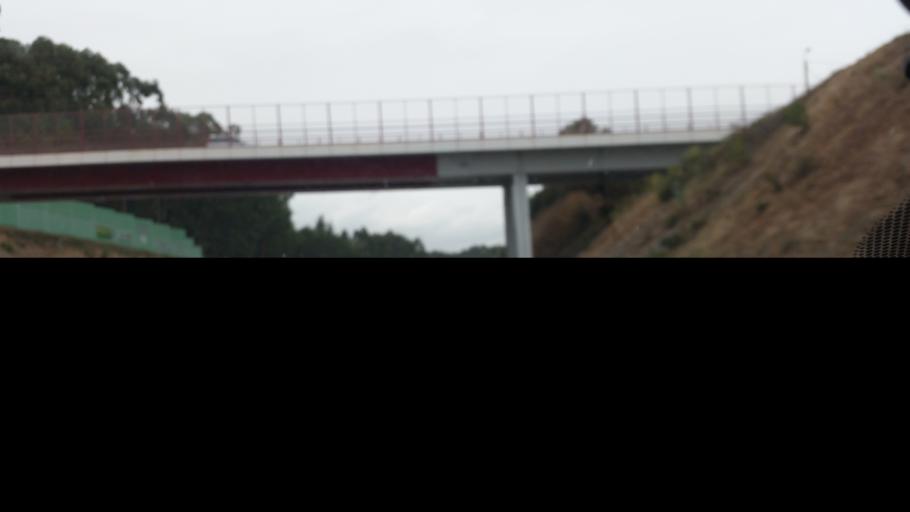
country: PT
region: Porto
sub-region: Trofa
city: Sao Romao do Coronado
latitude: 41.2840
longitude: -8.5593
